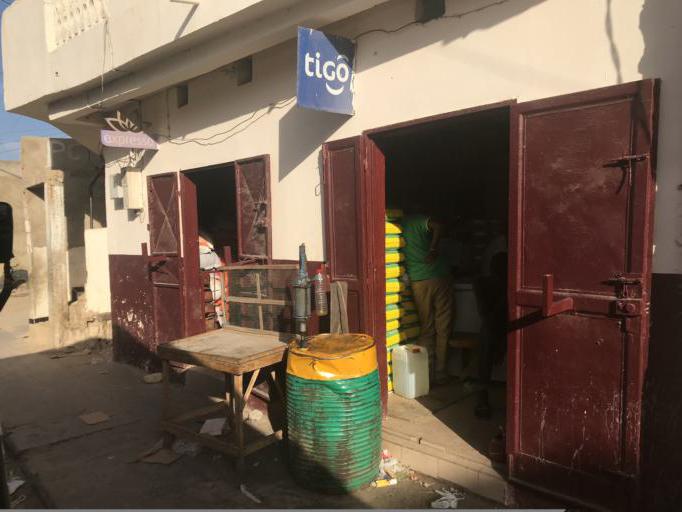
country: SN
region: Saint-Louis
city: Saint-Louis
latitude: 16.0046
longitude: -16.4953
